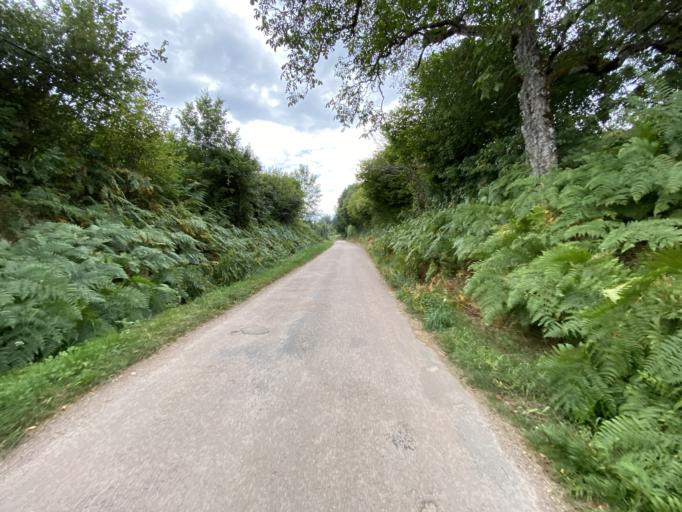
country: FR
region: Bourgogne
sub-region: Departement de la Cote-d'Or
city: Saulieu
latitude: 47.2606
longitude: 4.1367
